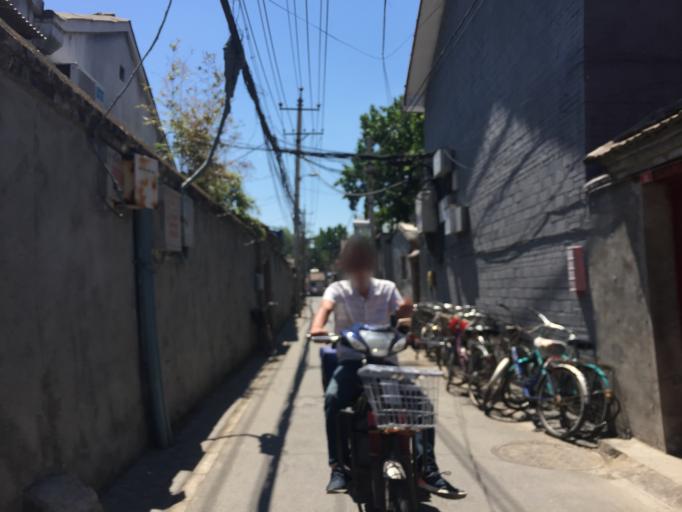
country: CN
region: Beijing
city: Jingshan
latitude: 39.9286
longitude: 116.3875
